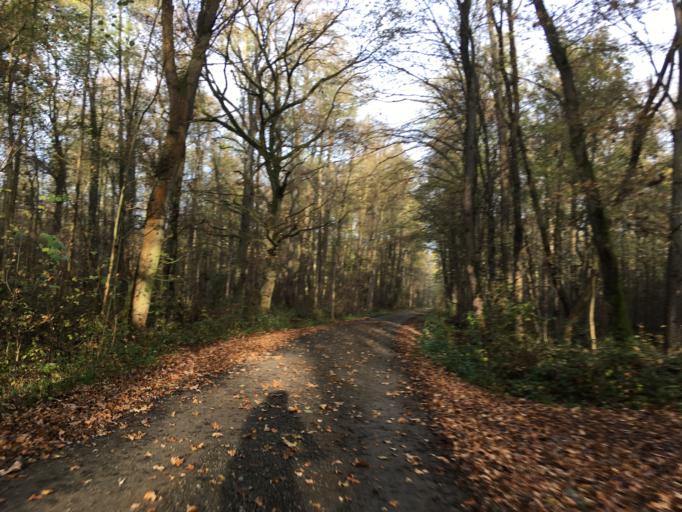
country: DE
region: Brandenburg
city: Schlepzig
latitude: 51.9936
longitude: 13.8729
